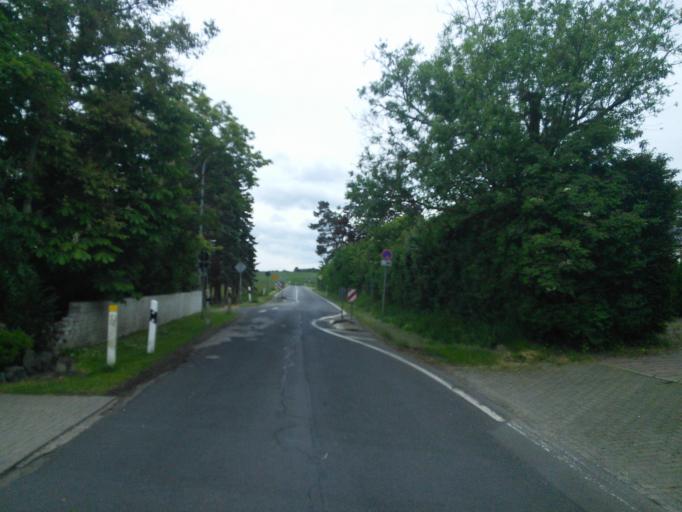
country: DE
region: Rheinland-Pfalz
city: Kirchsahr
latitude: 50.5568
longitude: 6.9009
